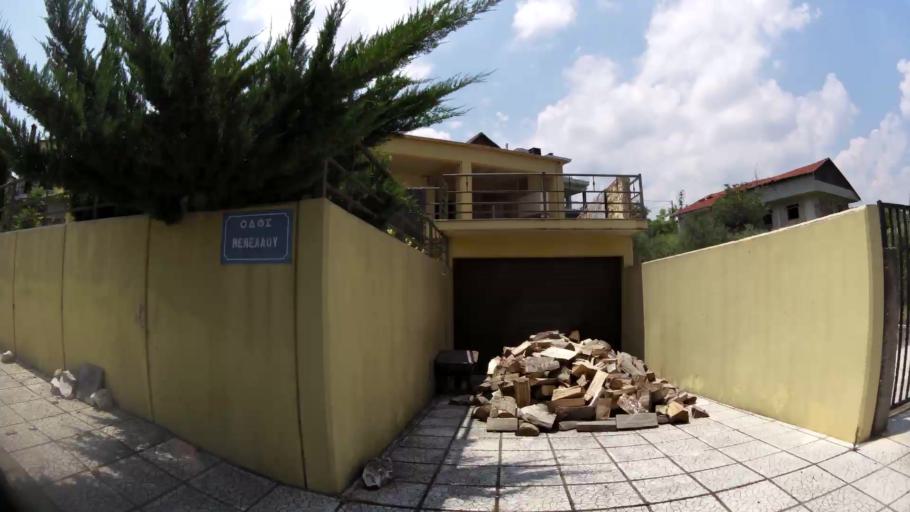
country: GR
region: Central Macedonia
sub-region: Nomos Imathias
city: Veroia
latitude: 40.5161
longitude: 22.1861
